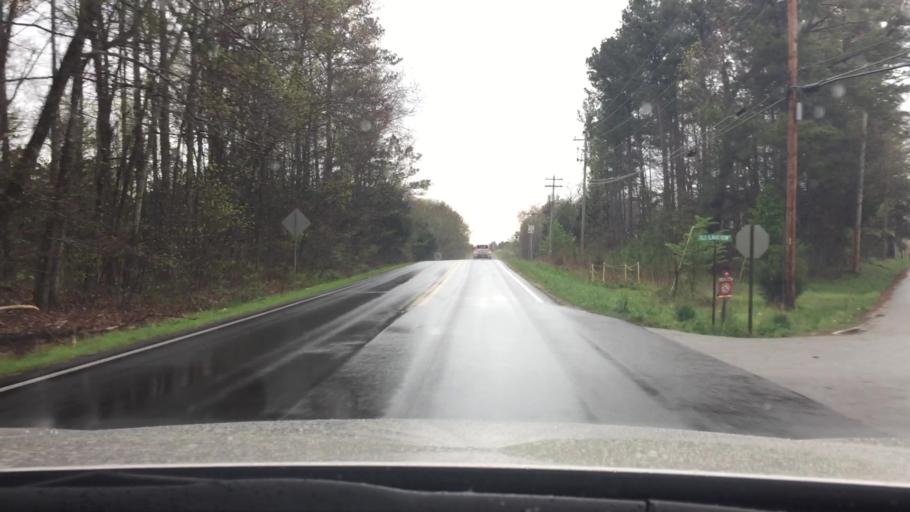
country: US
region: Georgia
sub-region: Catoosa County
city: Lakeview
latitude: 34.9730
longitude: -85.2380
